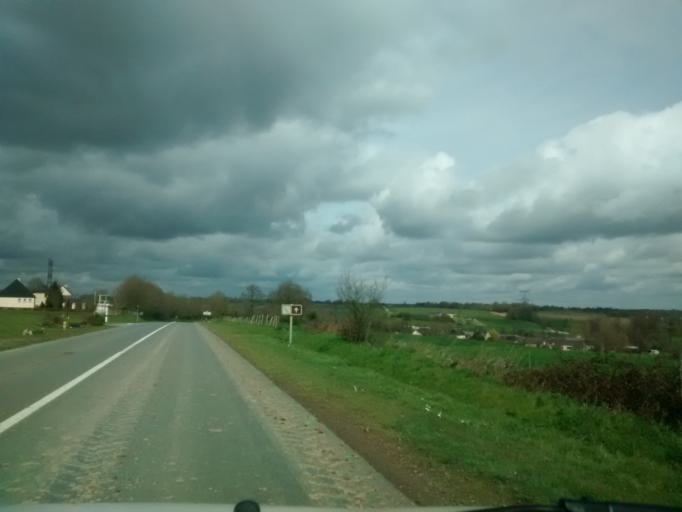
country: FR
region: Brittany
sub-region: Departement d'Ille-et-Vilaine
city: Livre-sur-Changeon
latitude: 48.2231
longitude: -1.3484
